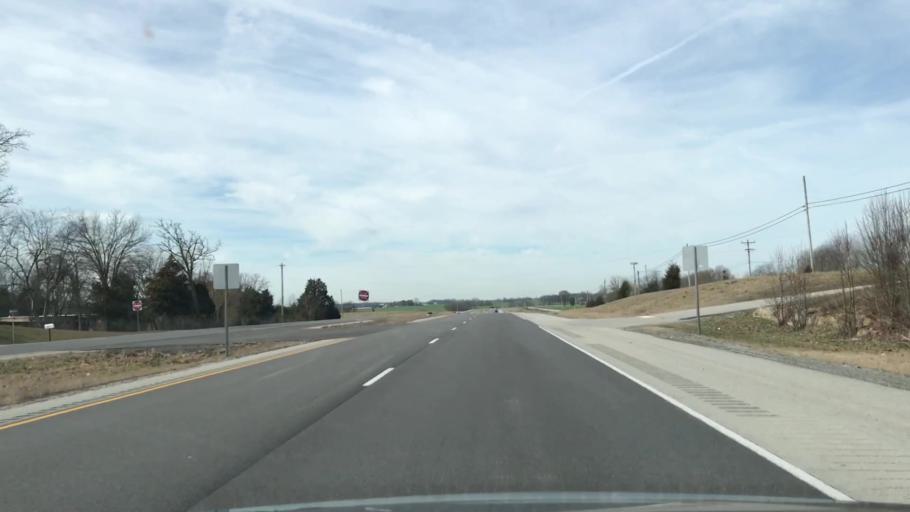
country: US
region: Kentucky
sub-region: Christian County
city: Hopkinsville
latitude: 36.8813
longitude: -87.6239
